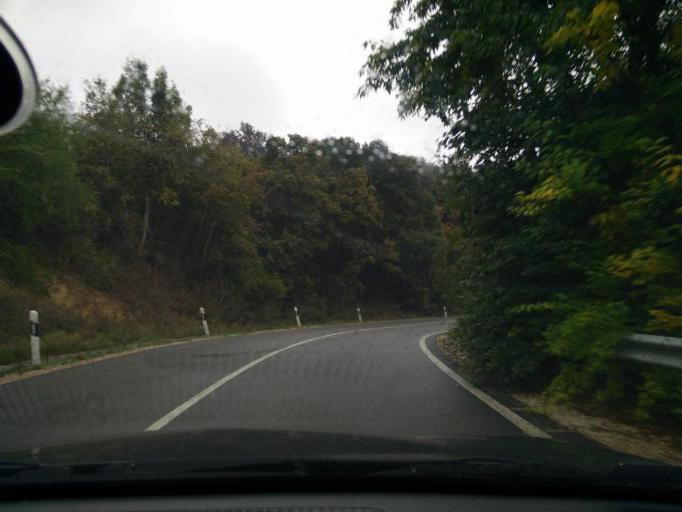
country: HU
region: Komarom-Esztergom
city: Tarjan
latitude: 47.6431
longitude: 18.5385
